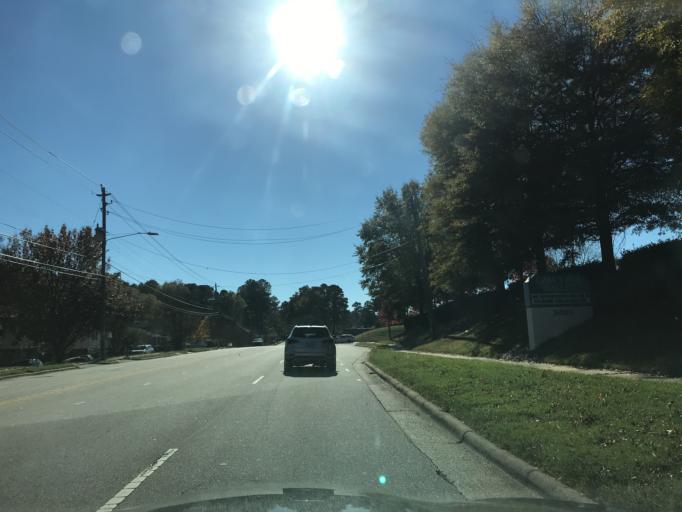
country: US
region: North Carolina
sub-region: Wake County
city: Raleigh
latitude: 35.8300
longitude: -78.6032
